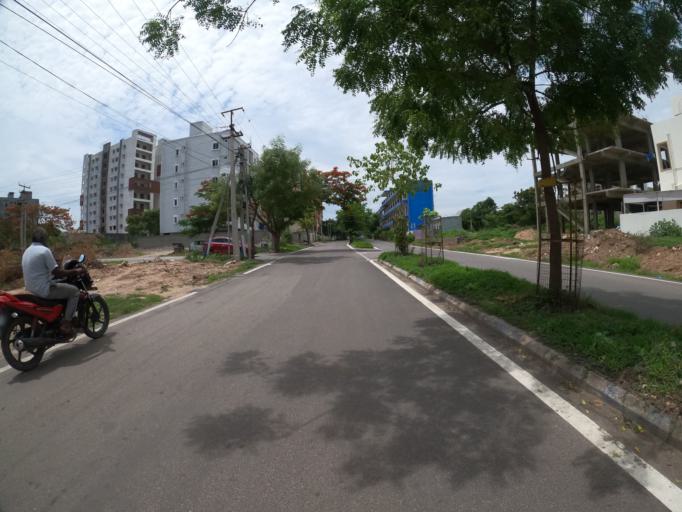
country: IN
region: Telangana
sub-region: Hyderabad
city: Hyderabad
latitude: 17.3683
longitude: 78.4144
